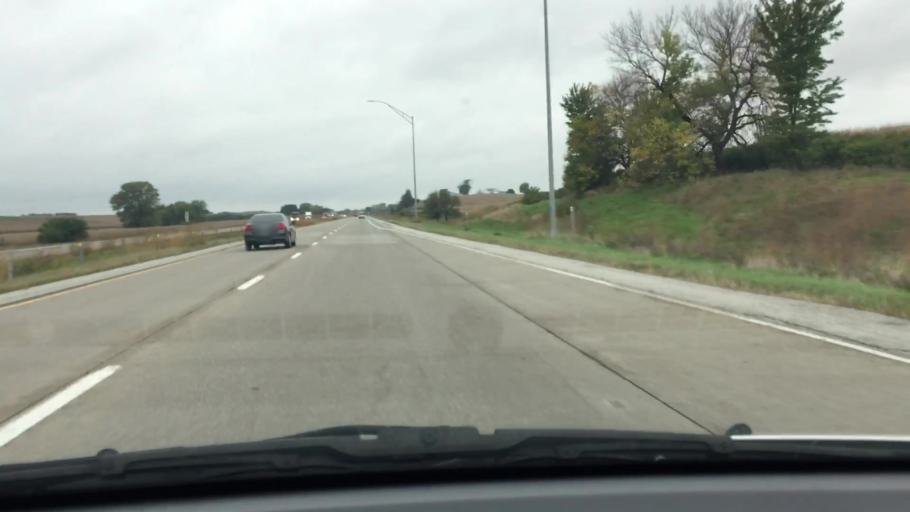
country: US
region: Iowa
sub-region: Iowa County
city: Williamsburg
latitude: 41.6880
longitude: -91.9187
